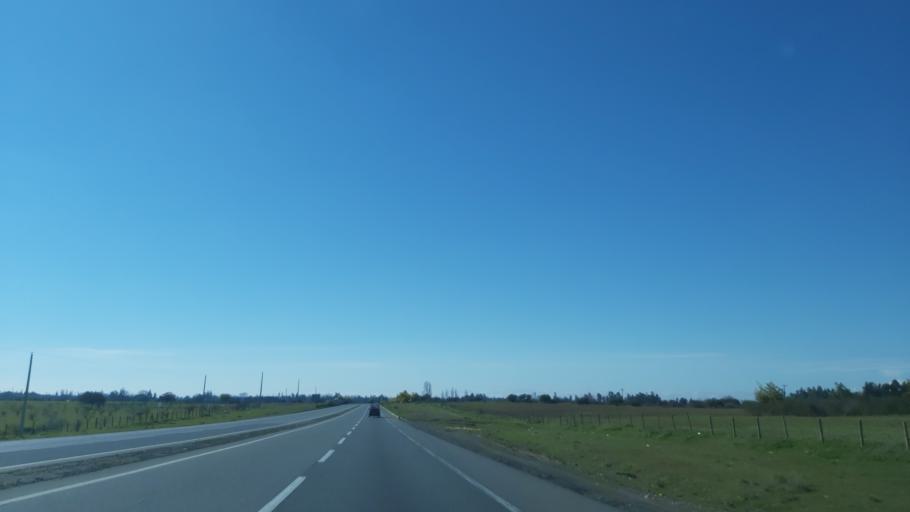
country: CL
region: Biobio
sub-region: Provincia de Nuble
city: Bulnes
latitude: -36.6573
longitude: -72.2479
